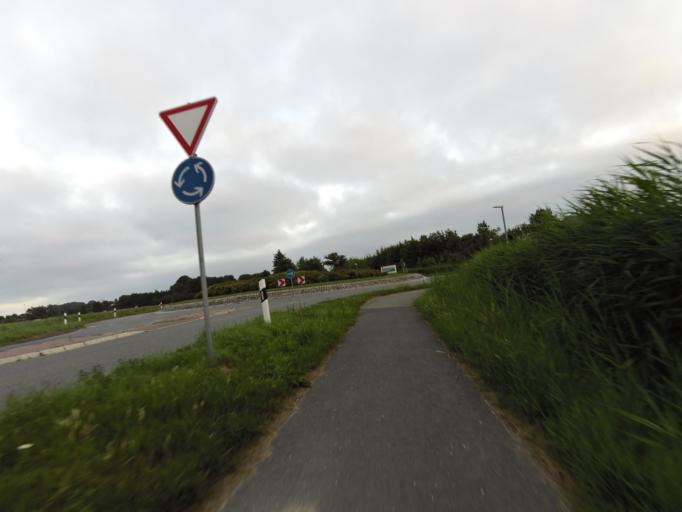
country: DE
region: Lower Saxony
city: Dorum
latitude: 53.6973
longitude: 8.5622
